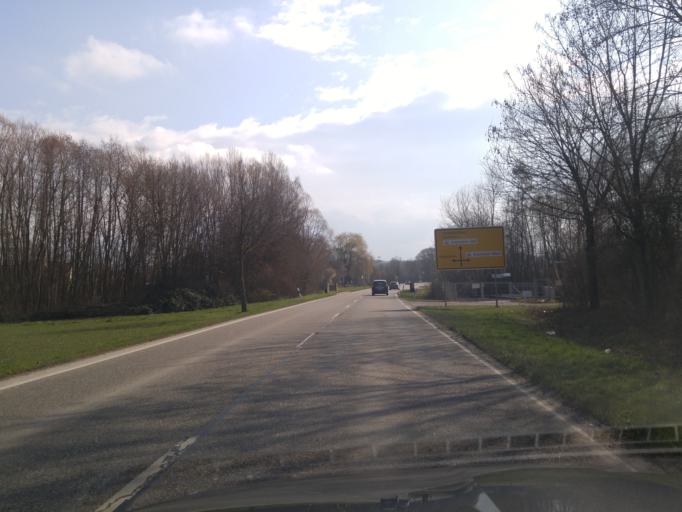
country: DE
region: Baden-Wuerttemberg
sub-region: Regierungsbezirk Stuttgart
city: Abstatt
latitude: 49.0569
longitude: 9.2746
